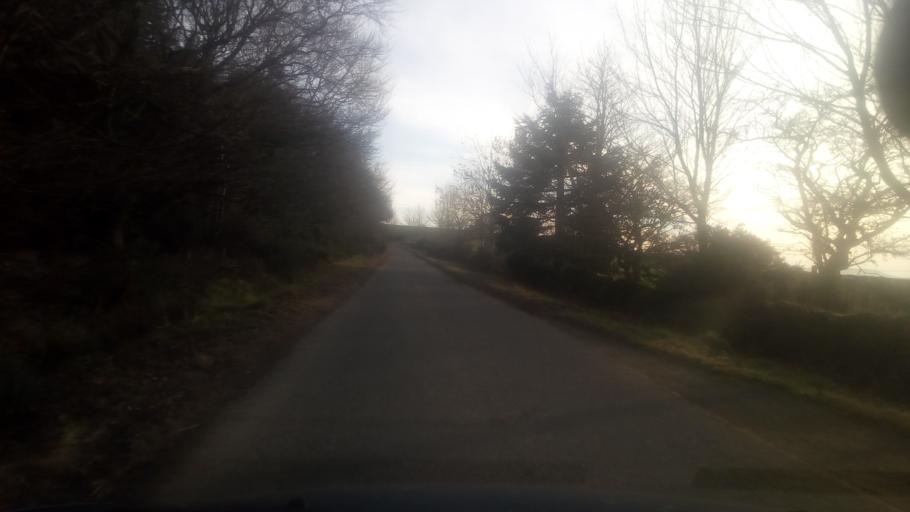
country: GB
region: Scotland
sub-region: The Scottish Borders
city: Jedburgh
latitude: 55.4051
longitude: -2.6007
